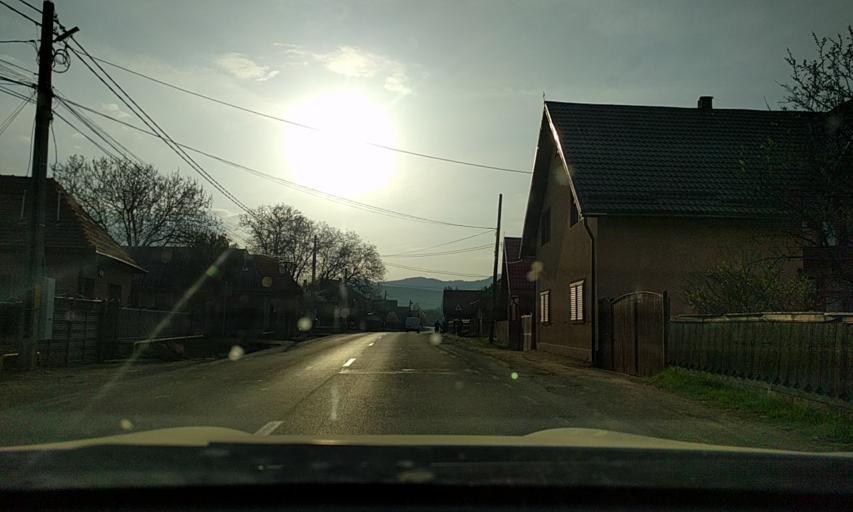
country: RO
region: Covasna
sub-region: Comuna Bretcu
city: Bretcu
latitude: 46.0414
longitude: 26.2912
